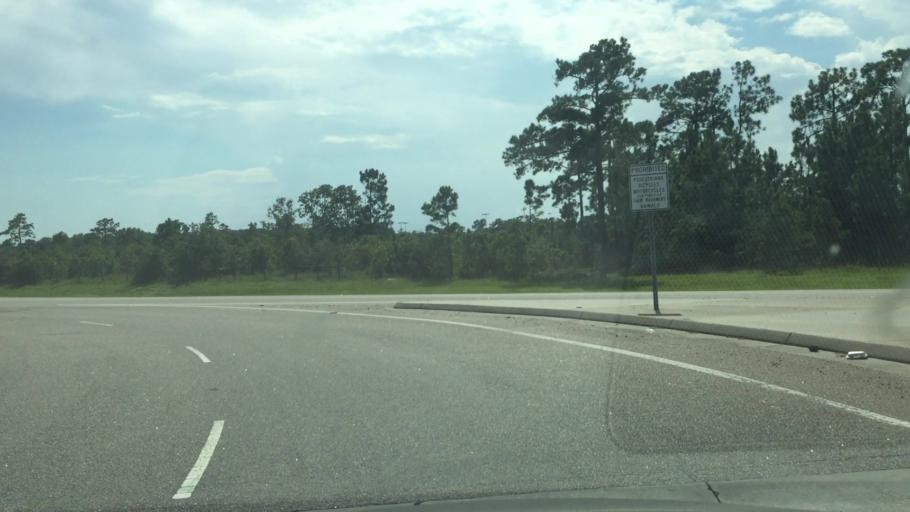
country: US
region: South Carolina
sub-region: Horry County
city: North Myrtle Beach
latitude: 33.8457
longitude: -78.7022
